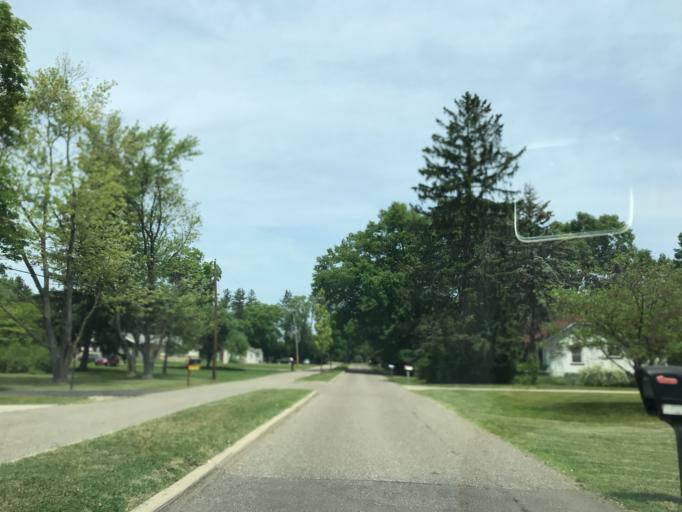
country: US
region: Michigan
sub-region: Oakland County
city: Bingham Farms
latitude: 42.4765
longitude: -83.2655
